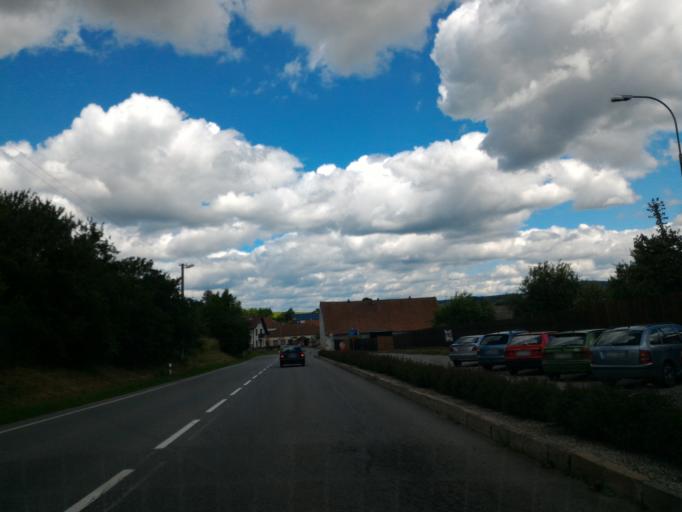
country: CZ
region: Vysocina
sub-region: Okres Jihlava
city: Trest'
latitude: 49.2686
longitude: 15.4764
